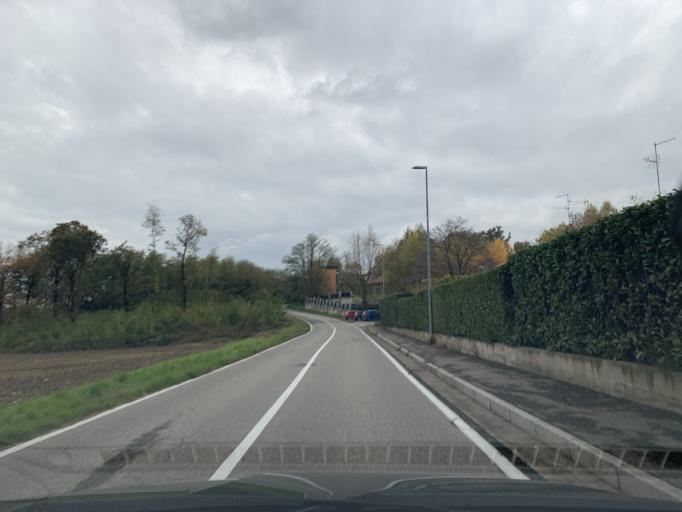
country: IT
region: Lombardy
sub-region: Provincia di Como
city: Casnate Con Bernate
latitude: 45.7514
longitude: 9.0711
